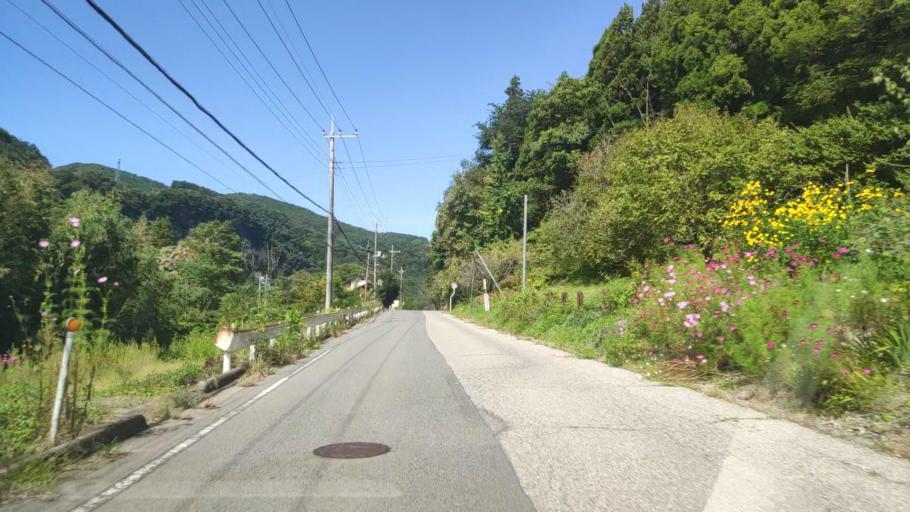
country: JP
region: Gunma
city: Numata
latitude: 36.5890
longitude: 139.0570
